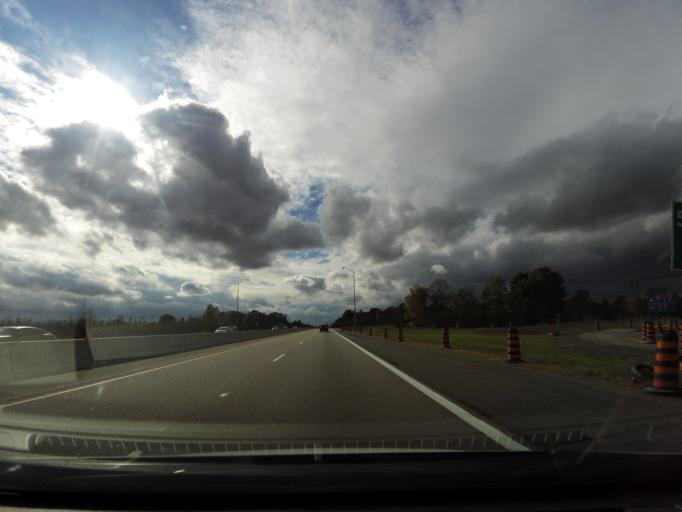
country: CA
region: Ontario
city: Belleville
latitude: 44.2197
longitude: -77.2439
